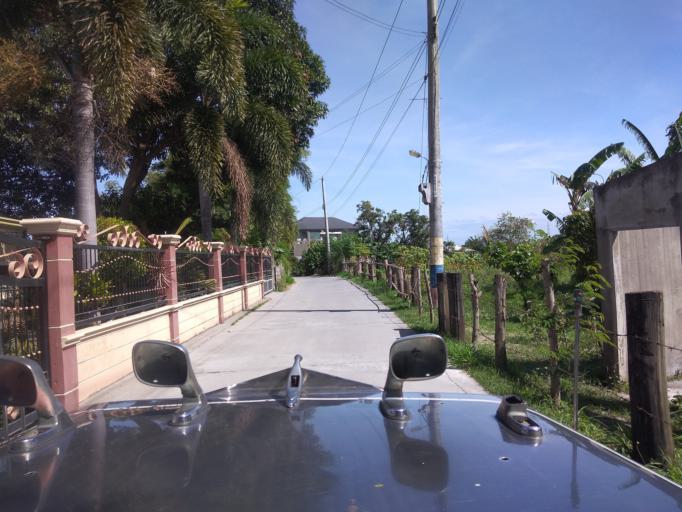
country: PH
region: Central Luzon
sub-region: Province of Pampanga
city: Magliman
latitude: 15.0264
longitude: 120.6533
